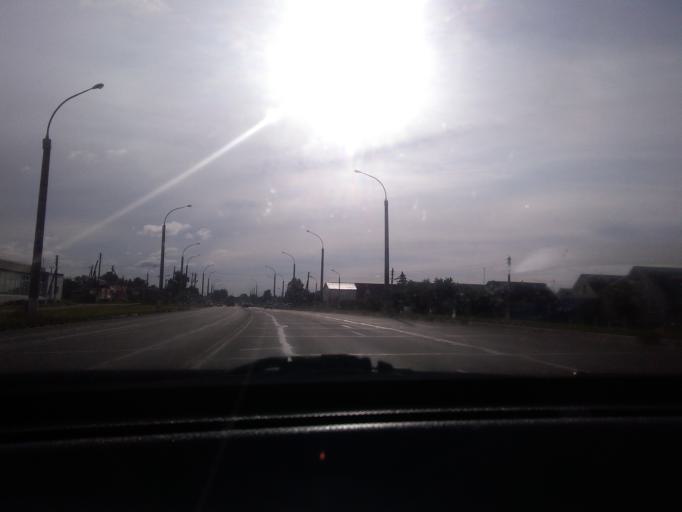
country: RU
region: Kursk
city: Pryamitsyno
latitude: 51.6555
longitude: 35.9265
